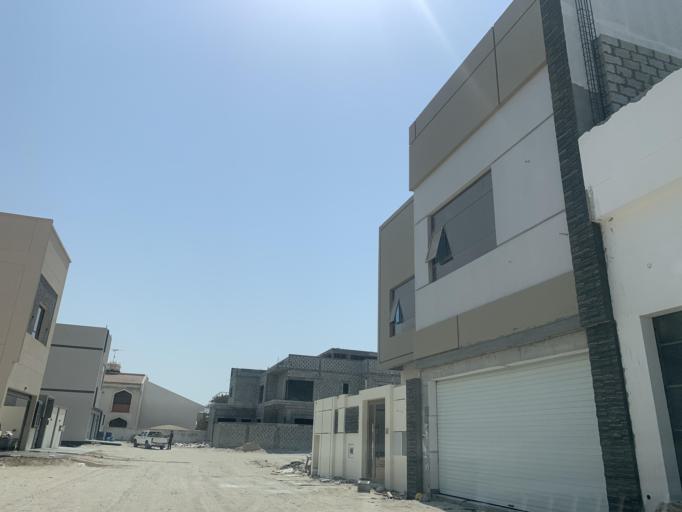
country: BH
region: Manama
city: Jidd Hafs
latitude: 26.2008
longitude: 50.5264
